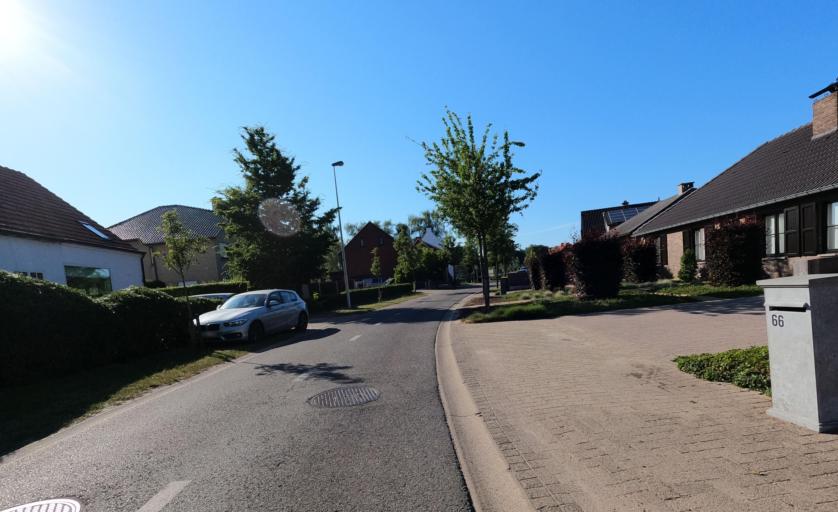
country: BE
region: Flanders
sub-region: Provincie Antwerpen
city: Schilde
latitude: 51.2684
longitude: 4.6297
